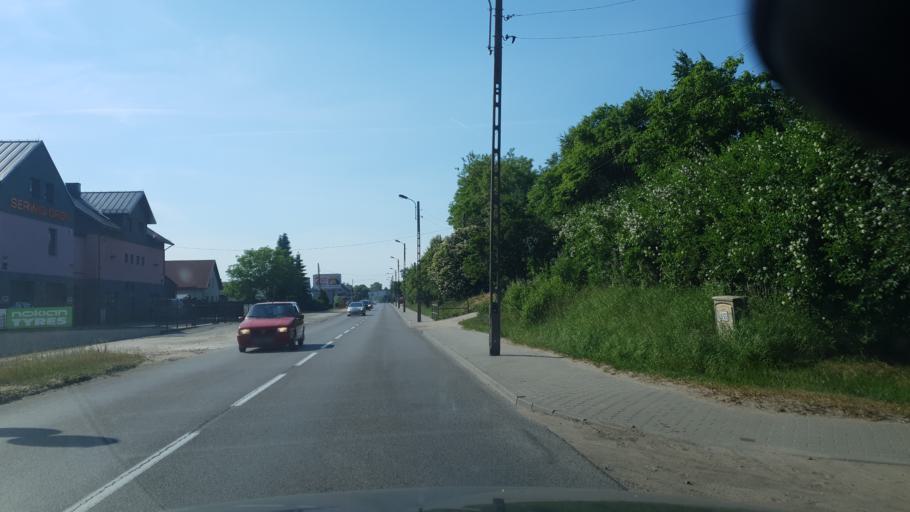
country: PL
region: Pomeranian Voivodeship
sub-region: Gdynia
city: Wielki Kack
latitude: 54.4384
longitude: 18.4611
